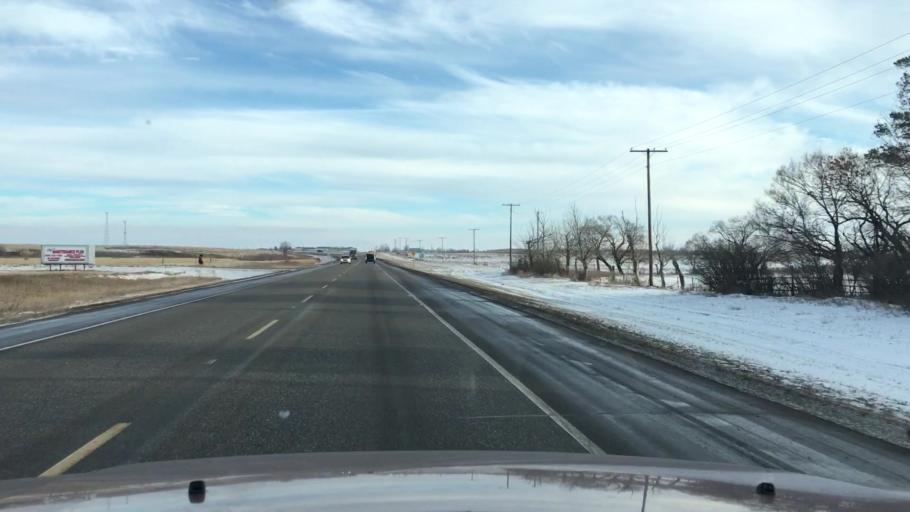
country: CA
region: Saskatchewan
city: Pilot Butte
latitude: 50.4844
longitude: -104.4479
